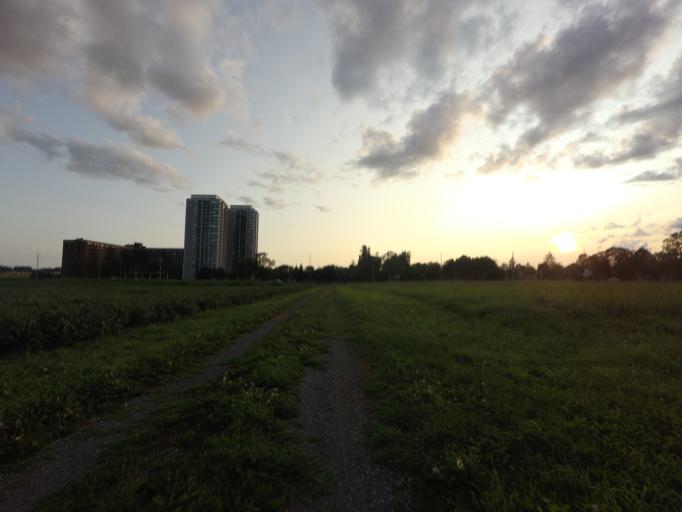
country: CA
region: Ontario
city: Ottawa
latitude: 45.3794
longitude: -75.7189
